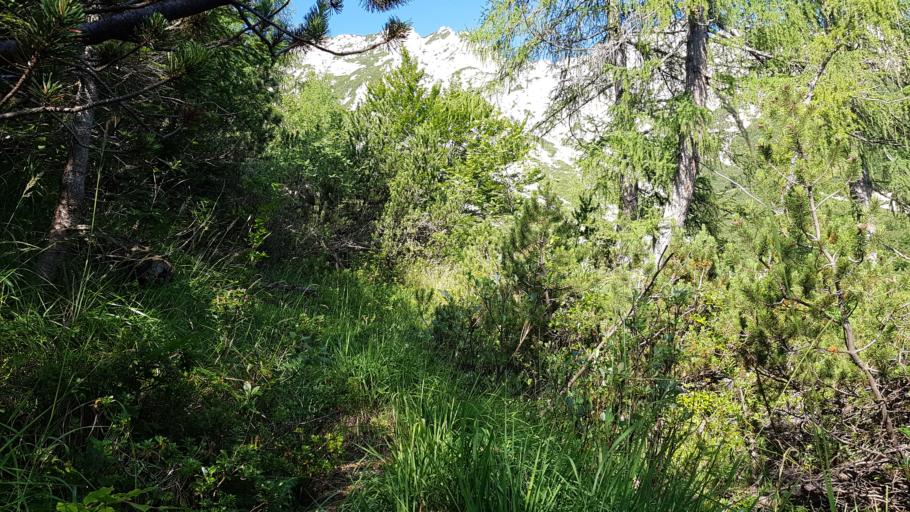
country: IT
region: Friuli Venezia Giulia
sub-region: Provincia di Udine
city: Pontebba
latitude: 46.4780
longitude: 13.2469
